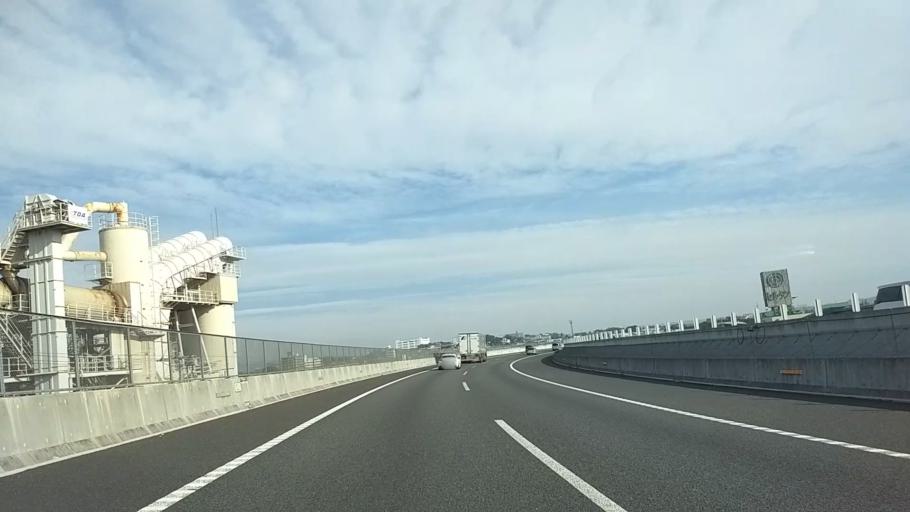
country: JP
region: Kanagawa
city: Atsugi
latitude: 35.4564
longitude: 139.3724
